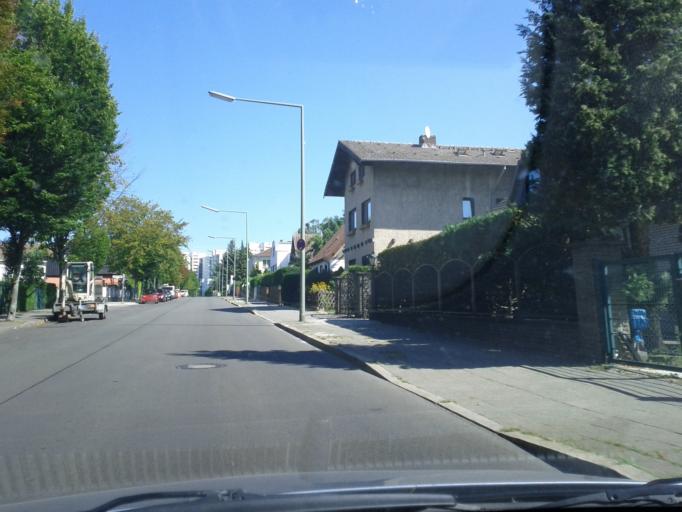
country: DE
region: Berlin
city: Markisches Viertel
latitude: 52.5924
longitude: 13.3465
